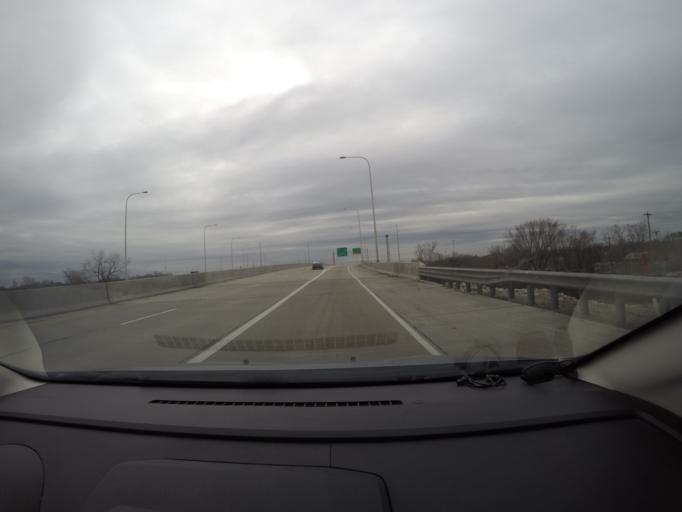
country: US
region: Illinois
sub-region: Saint Clair County
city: East Saint Louis
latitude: 38.6363
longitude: -90.1490
